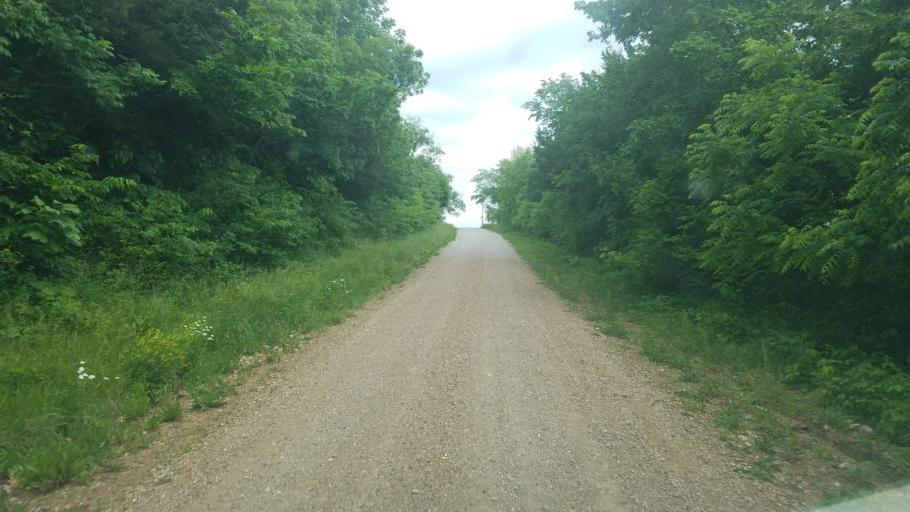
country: US
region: Missouri
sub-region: Moniteau County
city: California
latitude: 38.6218
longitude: -92.6233
